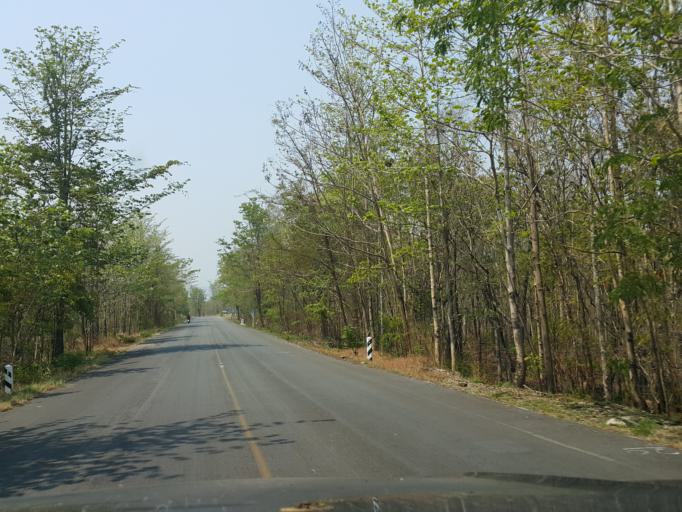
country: TH
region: Sukhothai
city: Thung Saliam
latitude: 17.4402
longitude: 99.3714
